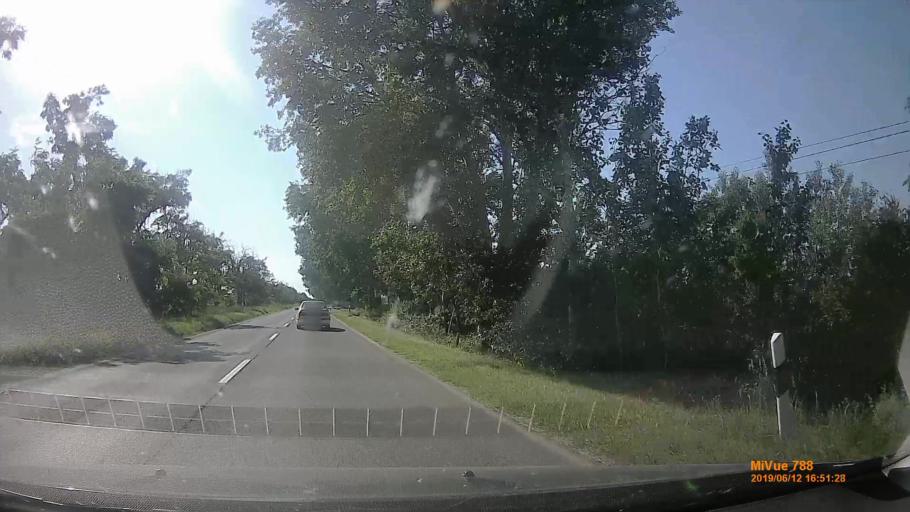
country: HU
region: Csongrad
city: Kiszombor
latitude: 46.2075
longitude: 20.3767
